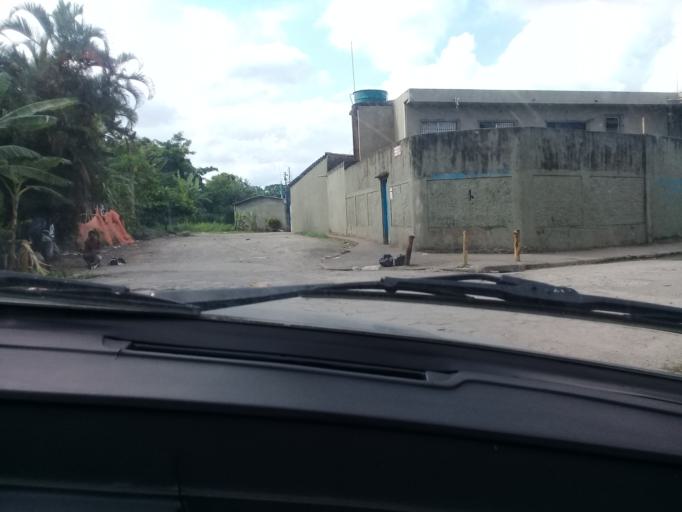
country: BR
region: Sao Paulo
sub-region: Guaruja
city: Guaruja
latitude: -23.9847
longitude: -46.2810
